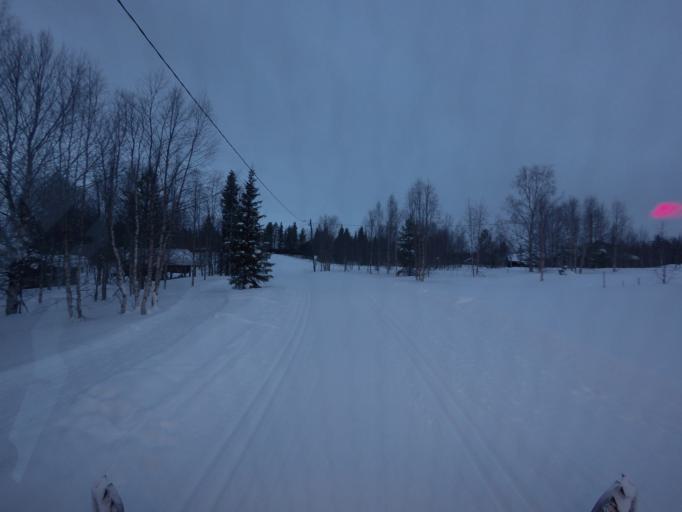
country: FI
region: Lapland
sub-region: Tunturi-Lappi
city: Kolari
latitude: 67.6160
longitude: 24.1610
